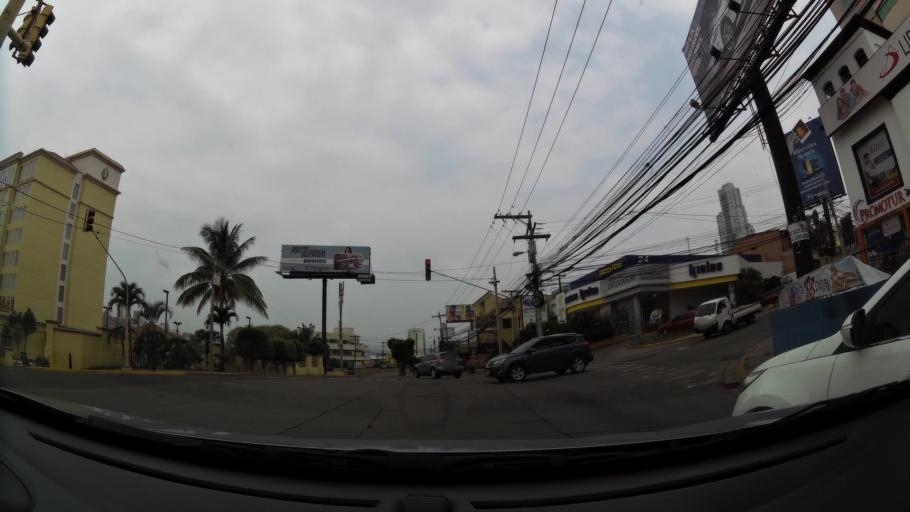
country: HN
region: Francisco Morazan
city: Tegucigalpa
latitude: 14.0892
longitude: -87.1843
